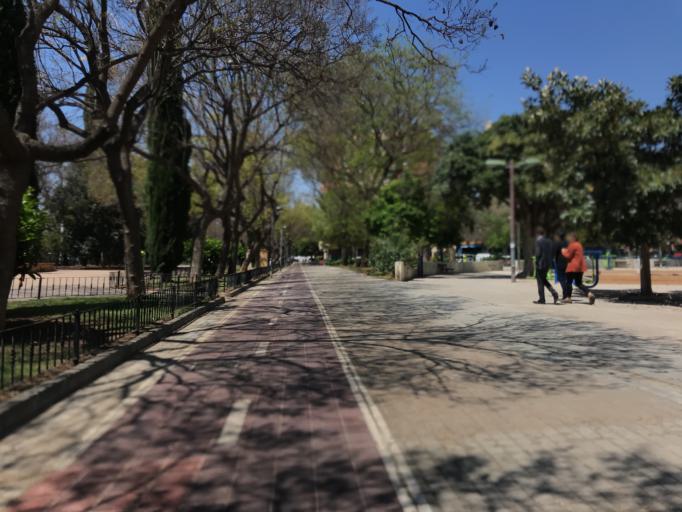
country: ES
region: Valencia
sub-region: Provincia de Valencia
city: Mislata
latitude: 39.4605
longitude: -0.4034
